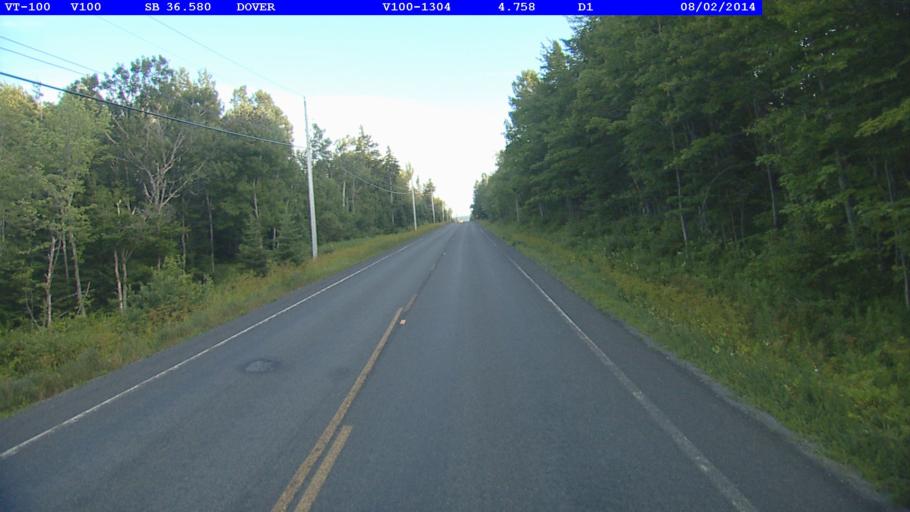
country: US
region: Vermont
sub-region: Windham County
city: Dover
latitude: 42.9798
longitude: -72.8885
